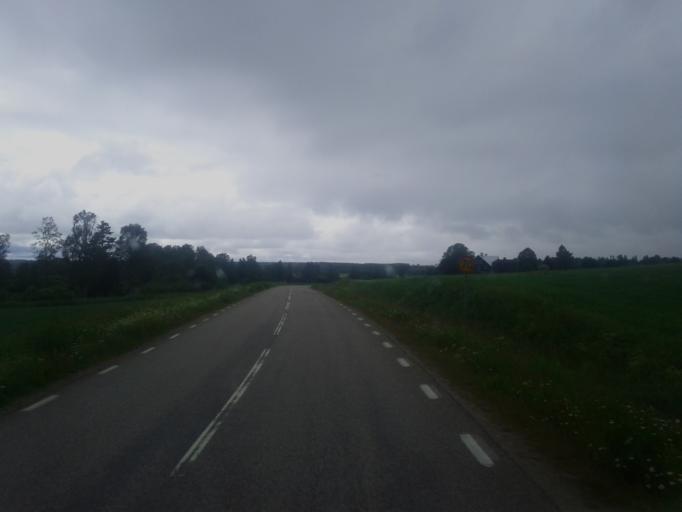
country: SE
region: Gaevleborg
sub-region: Nordanstigs Kommun
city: Bergsjoe
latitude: 61.9796
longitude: 17.2741
